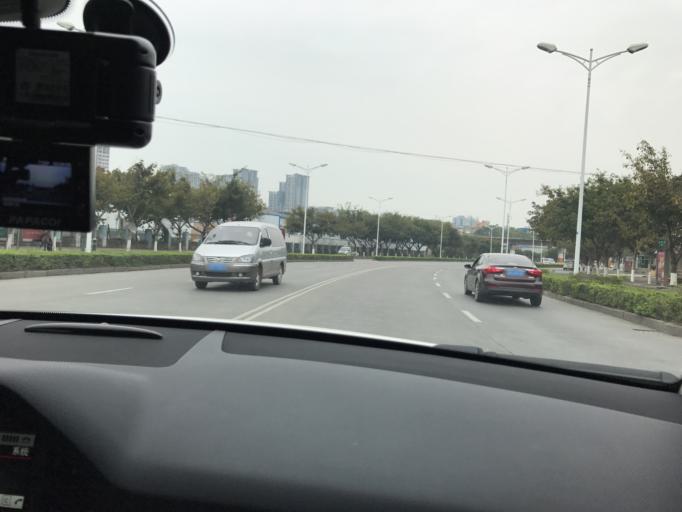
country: CN
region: Sichuan
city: Mianyang
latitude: 31.4593
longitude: 104.6740
